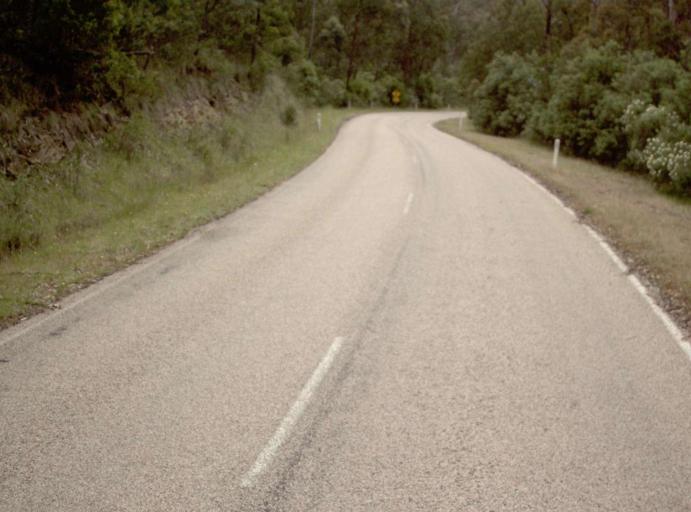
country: AU
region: Victoria
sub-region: East Gippsland
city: Bairnsdale
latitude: -37.5948
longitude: 147.1892
